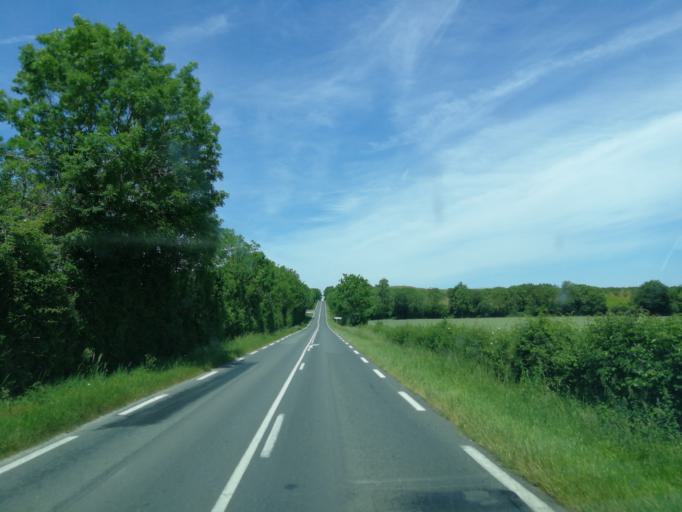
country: FR
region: Pays de la Loire
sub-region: Departement de la Vendee
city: Antigny
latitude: 46.6025
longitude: -0.7898
